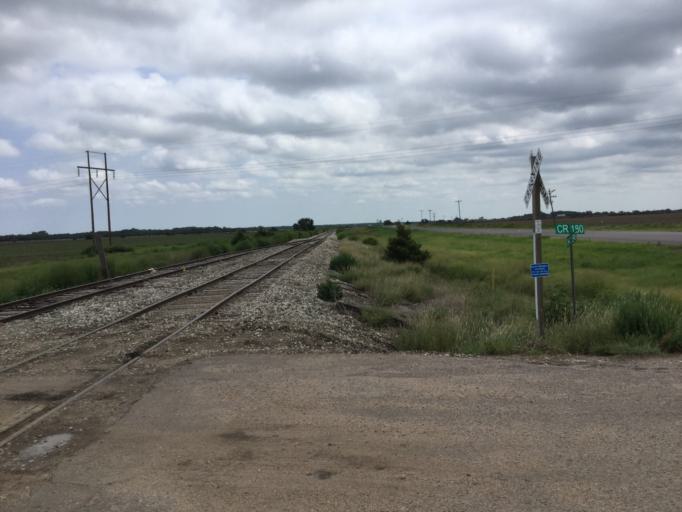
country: US
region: Kansas
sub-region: Rush County
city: La Crosse
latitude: 38.4730
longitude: -99.4379
